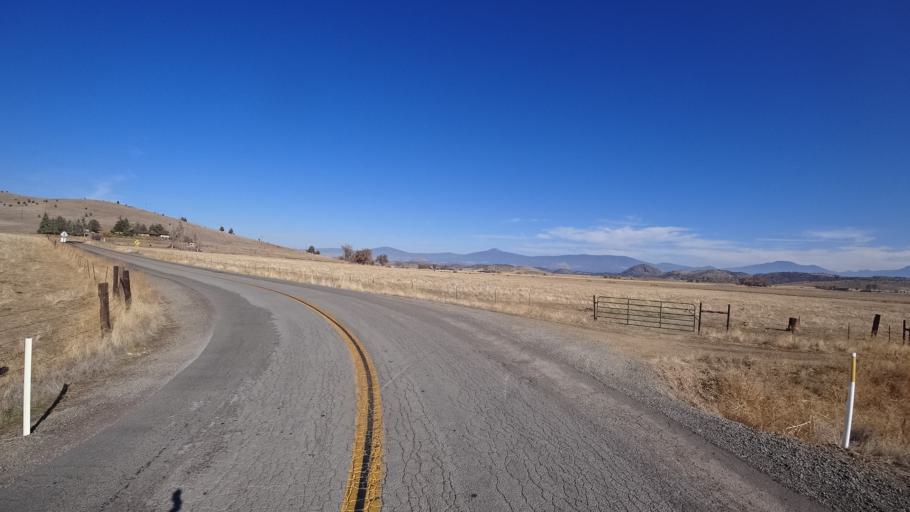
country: US
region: California
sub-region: Siskiyou County
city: Montague
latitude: 41.5971
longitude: -122.5350
